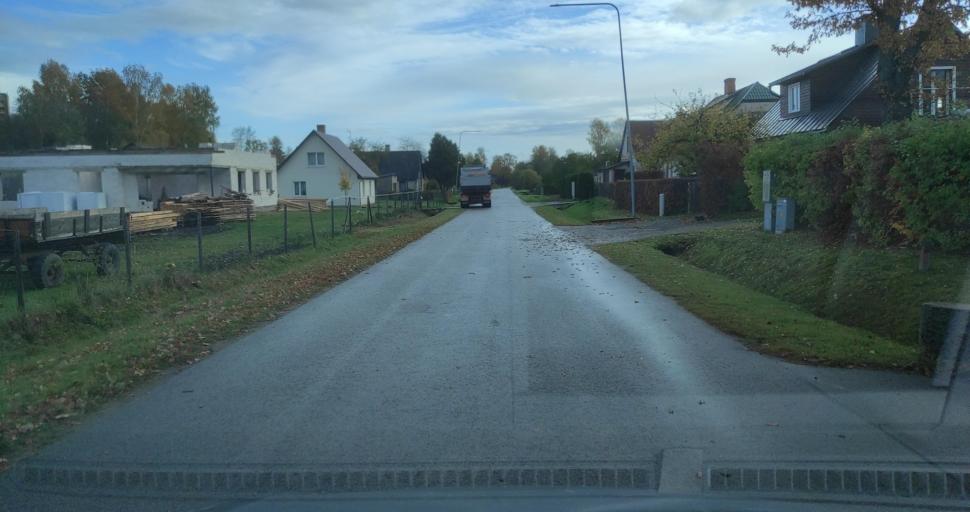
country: LV
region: Skrunda
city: Skrunda
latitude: 56.6713
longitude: 22.0021
